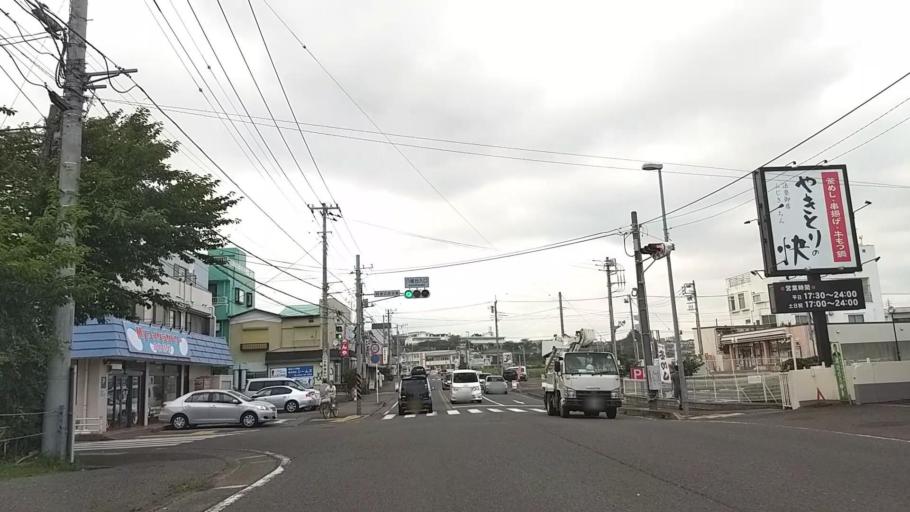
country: JP
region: Kanagawa
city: Isehara
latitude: 35.3848
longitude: 139.3162
